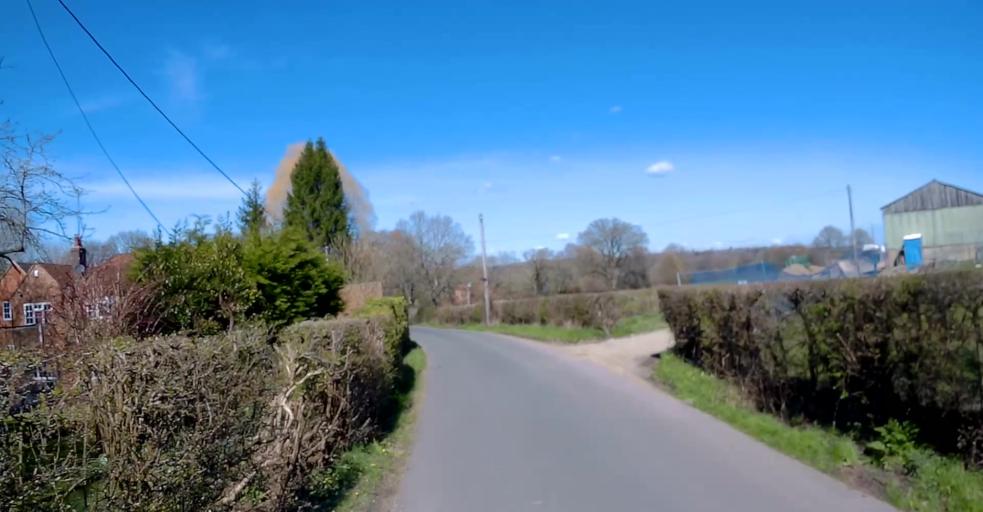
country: GB
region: England
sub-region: Hampshire
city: Lindford
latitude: 51.1655
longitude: -0.8286
